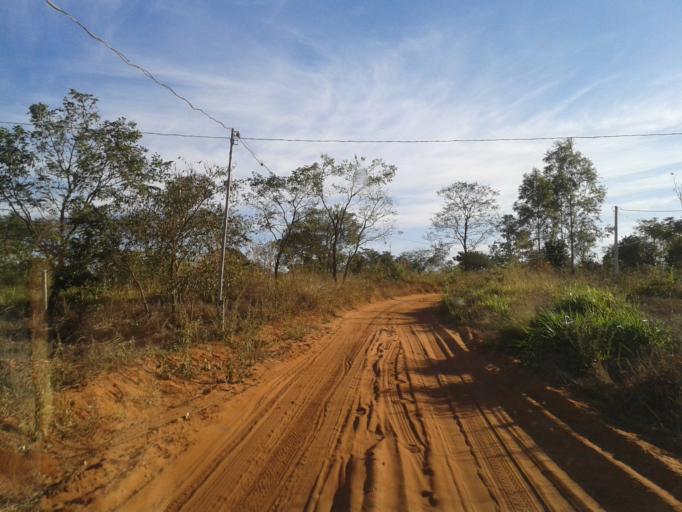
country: BR
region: Minas Gerais
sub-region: Santa Vitoria
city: Santa Vitoria
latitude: -19.0005
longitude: -50.3824
